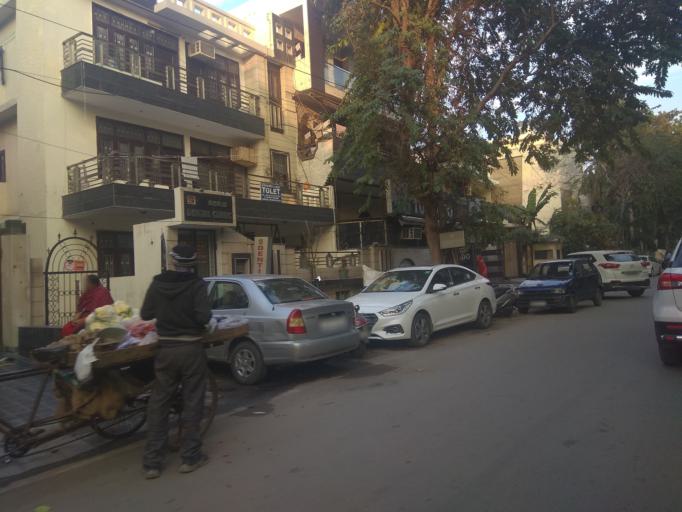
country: IN
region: NCT
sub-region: West Delhi
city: Nangloi Jat
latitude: 28.6316
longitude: 77.0723
